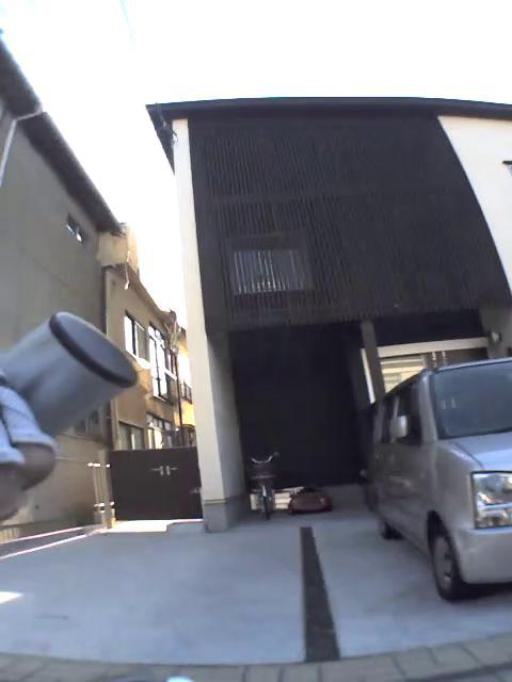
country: JP
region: Yamaguchi
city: Nagato
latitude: 34.3963
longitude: 131.1985
